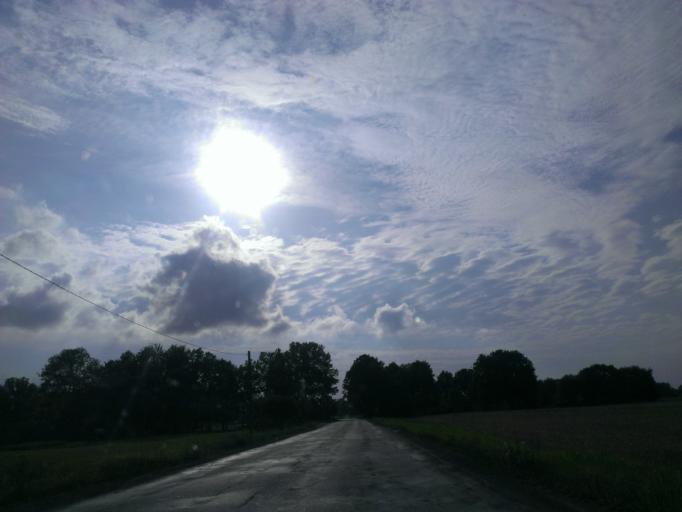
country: LV
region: Priekuli
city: Priekuli
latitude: 57.3122
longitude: 25.3240
